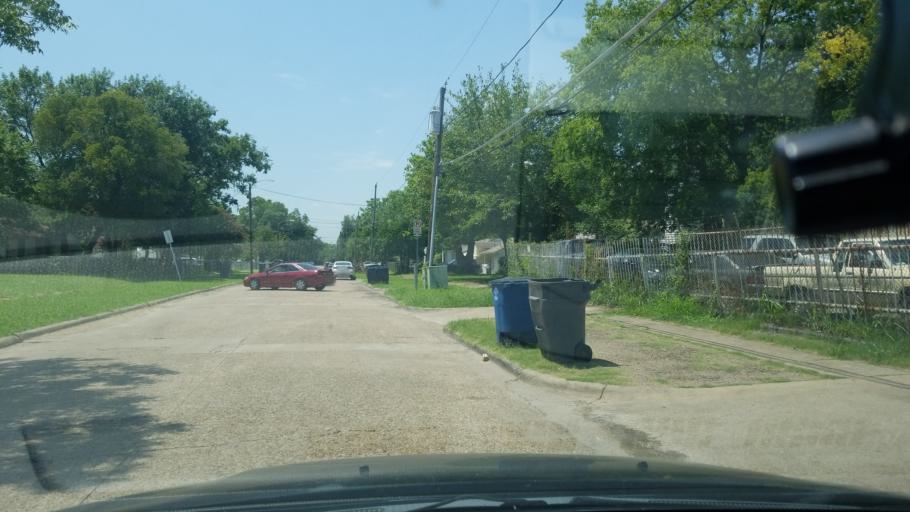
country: US
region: Texas
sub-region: Dallas County
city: Balch Springs
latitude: 32.7340
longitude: -96.6902
